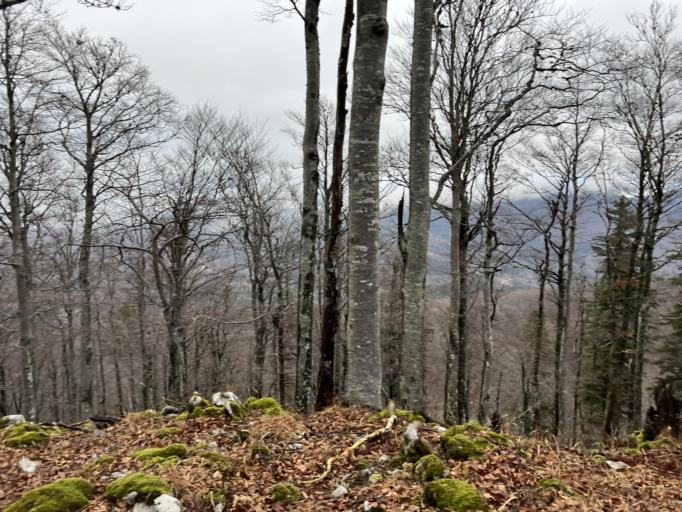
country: SI
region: Ajdovscina
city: Lokavec
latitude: 45.9519
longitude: 13.8341
